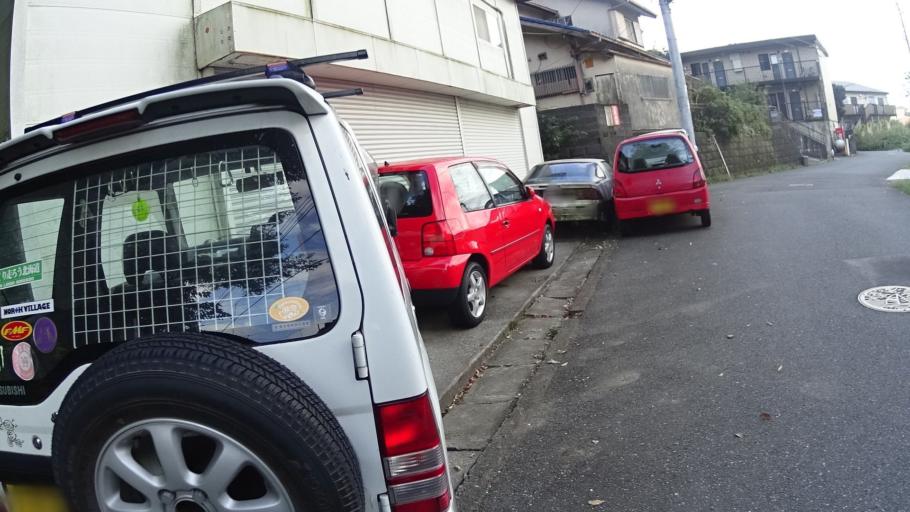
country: JP
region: Kanagawa
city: Zushi
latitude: 35.2855
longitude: 139.5926
